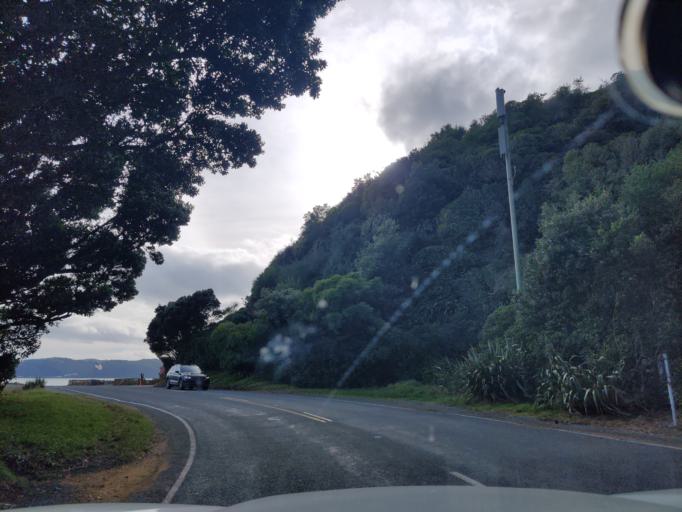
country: NZ
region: Wellington
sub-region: Wellington City
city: Wellington
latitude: -41.2983
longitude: 174.8207
